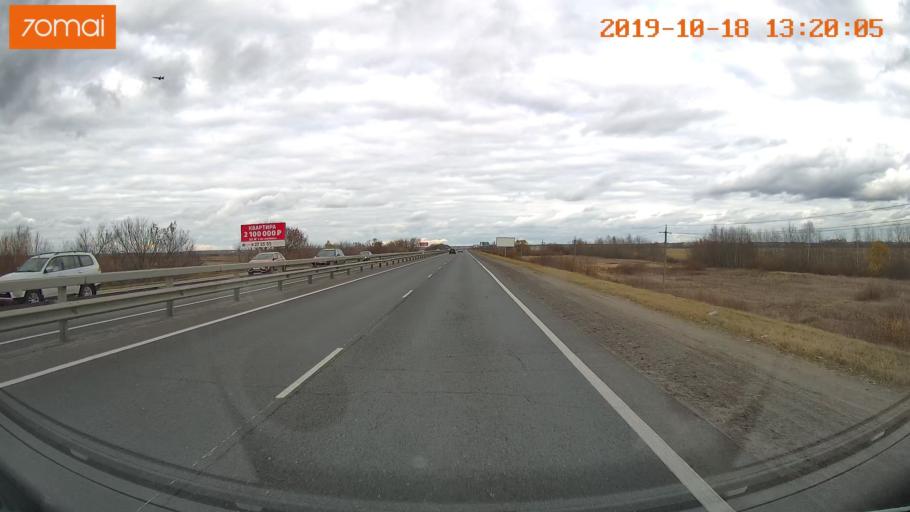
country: RU
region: Rjazan
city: Polyany
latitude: 54.6749
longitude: 39.8288
